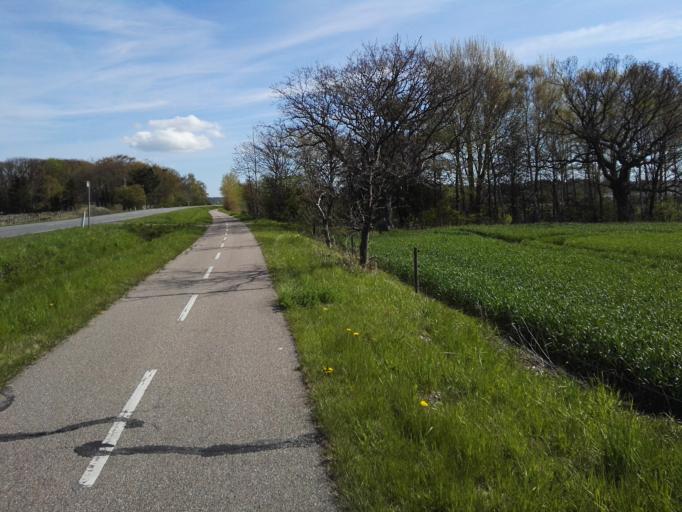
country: DK
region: Capital Region
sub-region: Halsnaes Kommune
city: Liseleje
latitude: 55.9665
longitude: 11.9677
